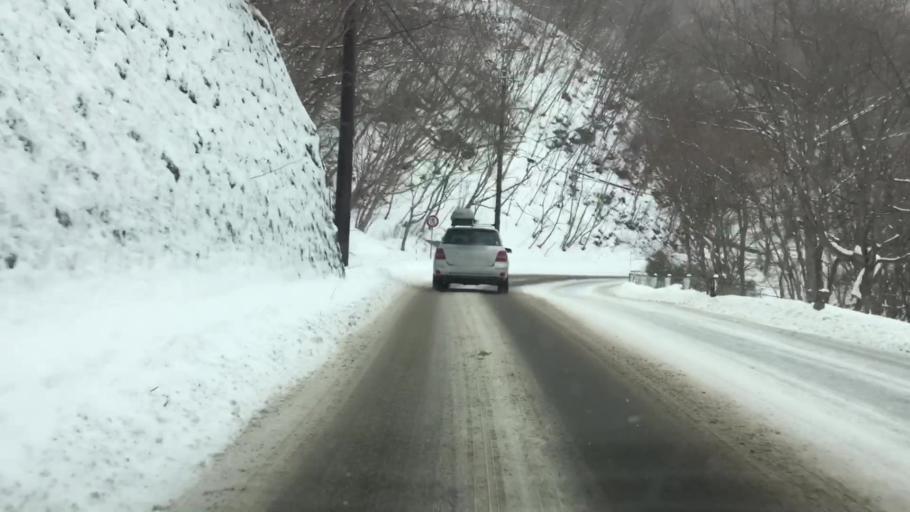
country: JP
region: Tochigi
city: Yaita
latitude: 36.9624
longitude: 139.7847
